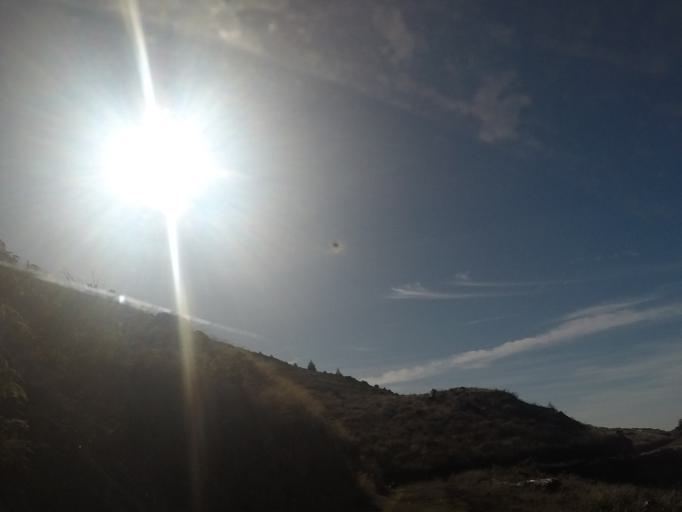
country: PT
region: Madeira
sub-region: Funchal
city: Nossa Senhora do Monte
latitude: 32.7078
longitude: -16.9000
